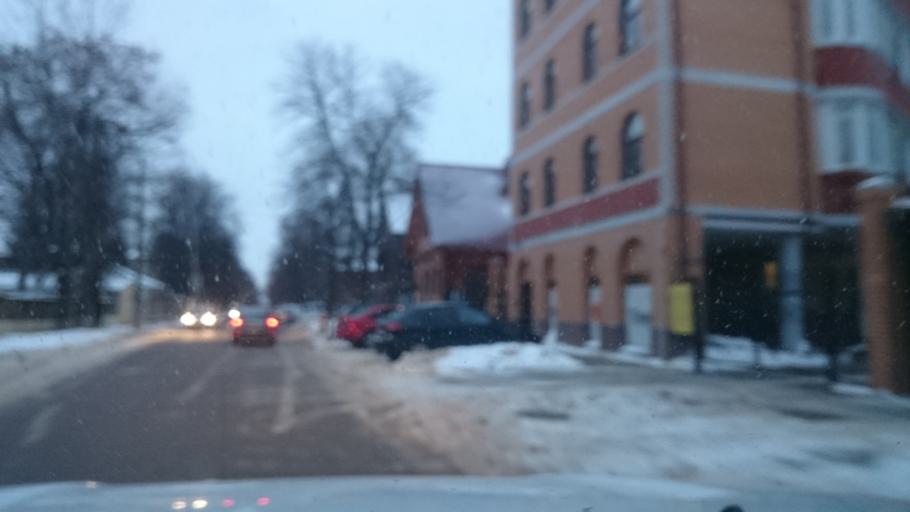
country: RU
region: Tula
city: Tula
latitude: 54.1842
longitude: 37.6007
